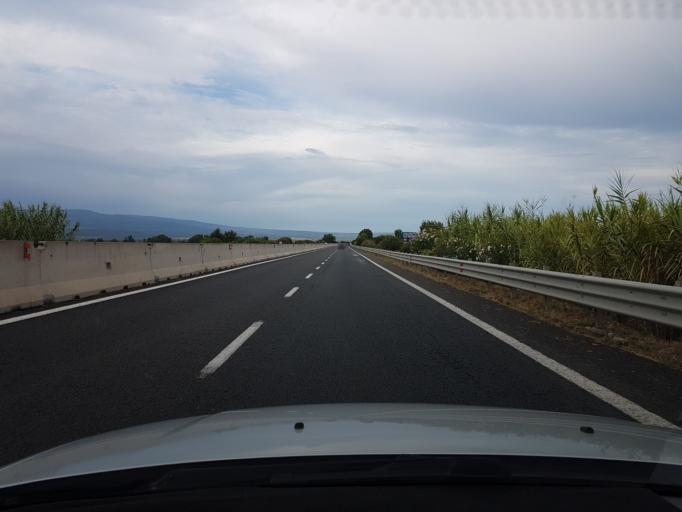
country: IT
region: Sardinia
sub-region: Provincia di Oristano
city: Siamaggiore
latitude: 39.9772
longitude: 8.6291
